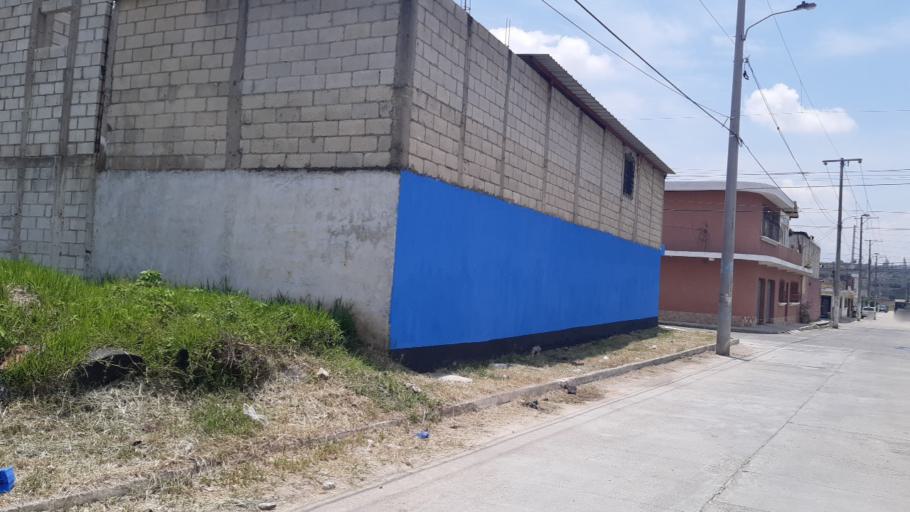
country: GT
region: Guatemala
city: Petapa
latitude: 14.5101
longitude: -90.5597
